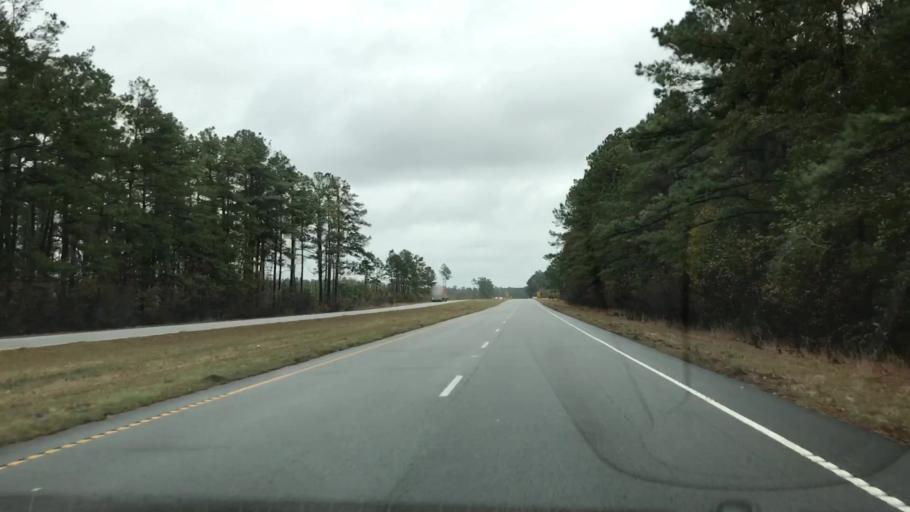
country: US
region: South Carolina
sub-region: Charleston County
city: Awendaw
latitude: 33.1679
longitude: -79.4212
